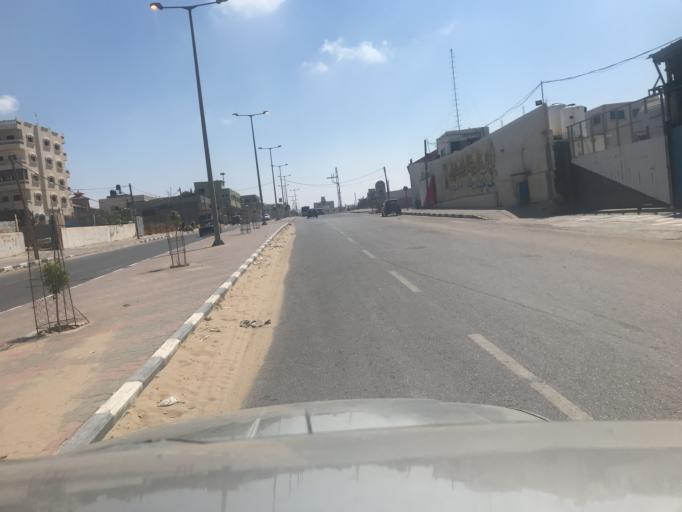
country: PS
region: Gaza Strip
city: Bayt Lahya
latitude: 31.5537
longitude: 34.4680
